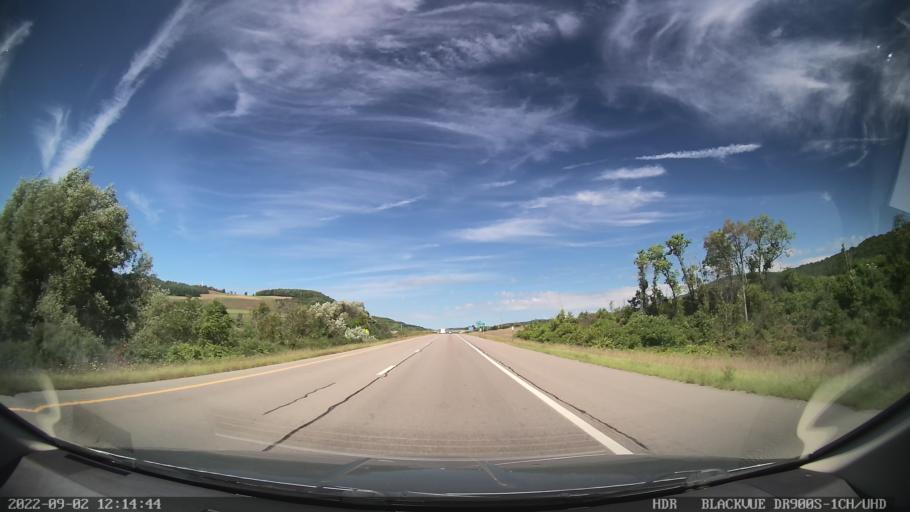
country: US
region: New York
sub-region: Steuben County
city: Wayland
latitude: 42.4569
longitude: -77.4790
